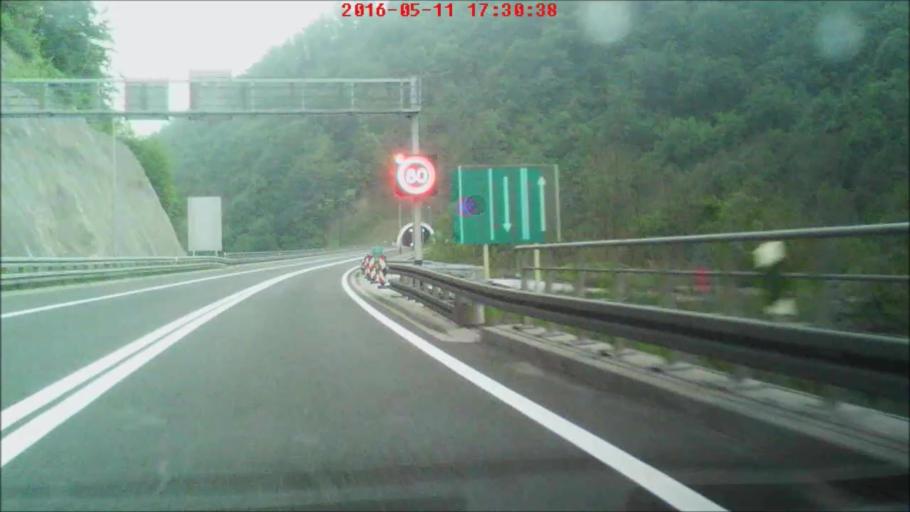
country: HR
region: Krapinsko-Zagorska
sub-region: Grad Krapina
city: Krapina
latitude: 46.1926
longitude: 15.8463
